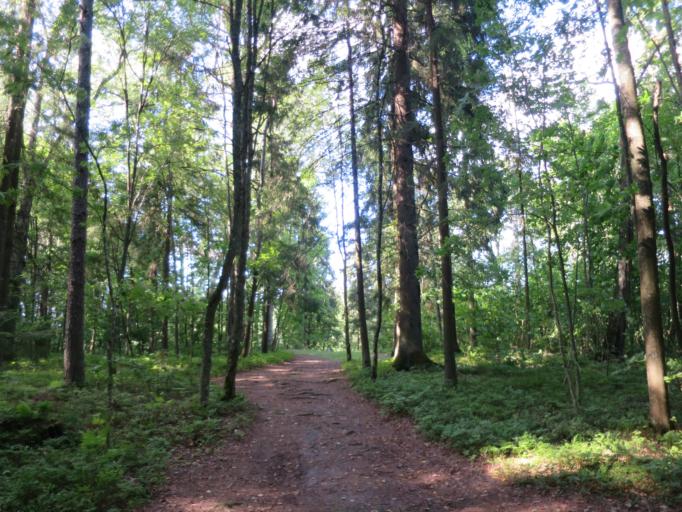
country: LV
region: Sigulda
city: Sigulda
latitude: 57.1707
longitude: 24.8759
